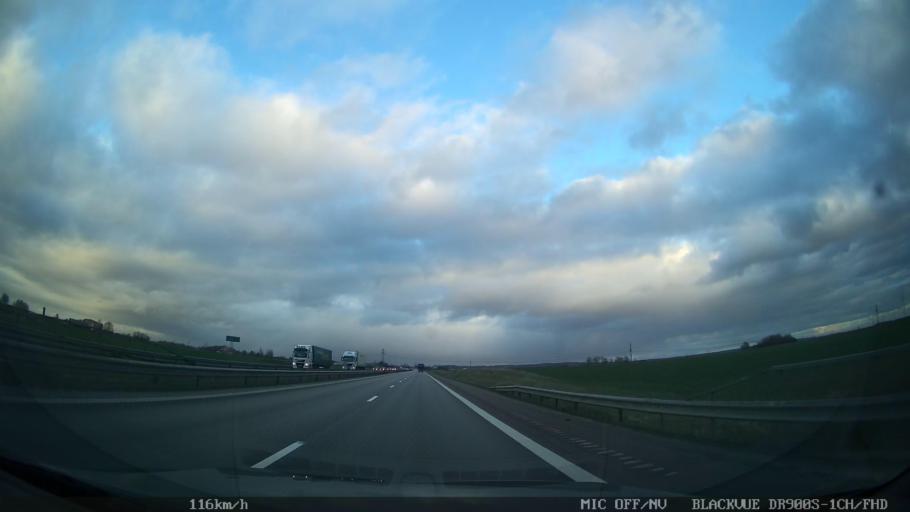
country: SE
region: Skane
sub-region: Helsingborg
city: Hyllinge
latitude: 56.1126
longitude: 12.8758
